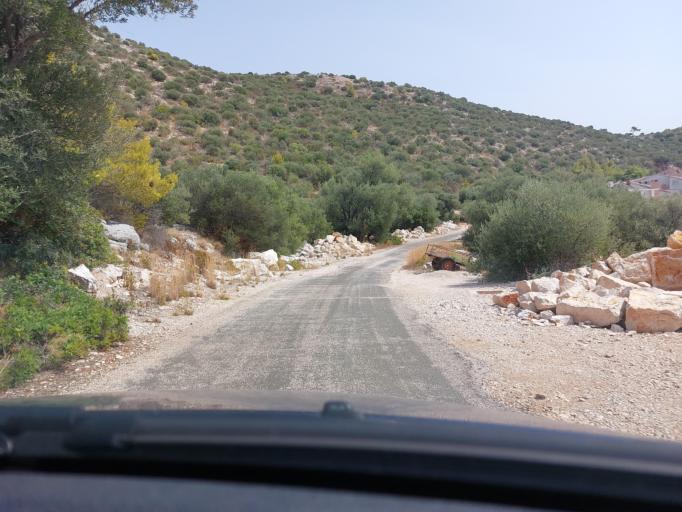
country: HR
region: Dubrovacko-Neretvanska
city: Smokvica
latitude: 42.7343
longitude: 16.8916
